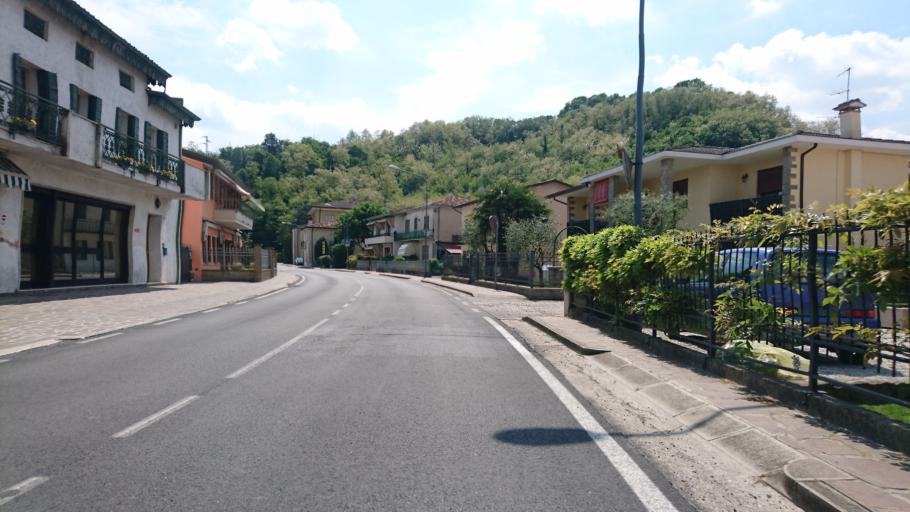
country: IT
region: Veneto
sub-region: Provincia di Padova
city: Montemerlo
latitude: 45.3804
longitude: 11.7049
